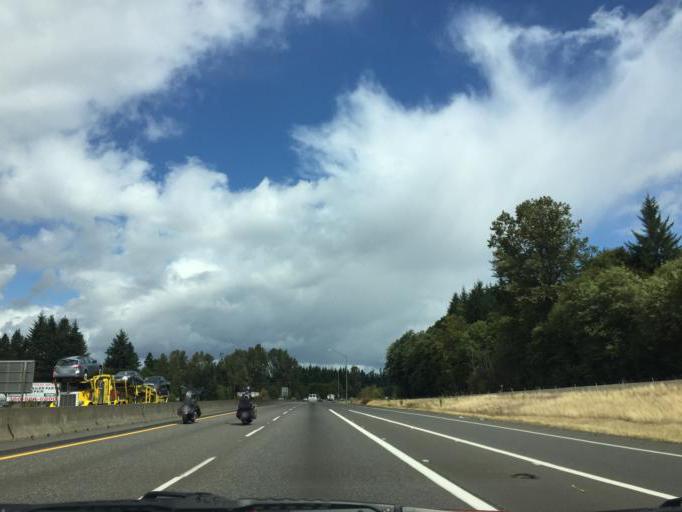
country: US
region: Washington
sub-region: Lewis County
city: Winlock
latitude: 46.3948
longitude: -122.9006
